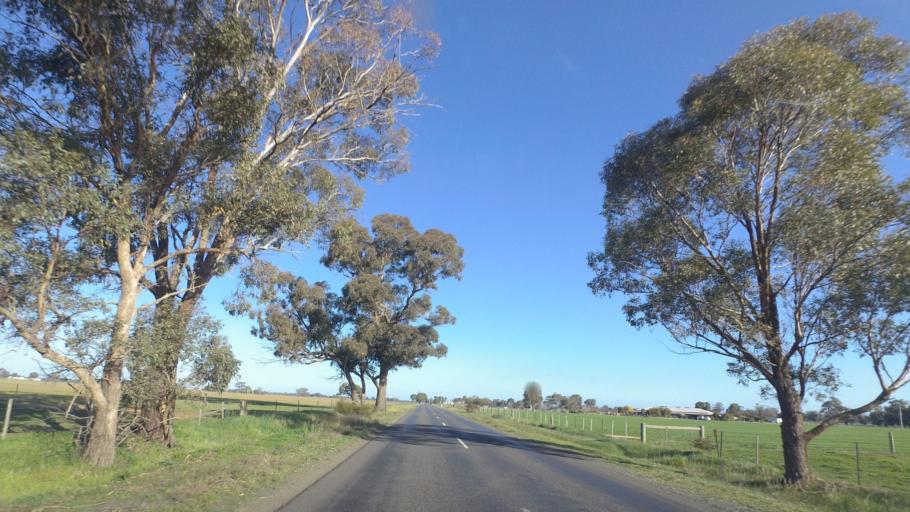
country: AU
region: Victoria
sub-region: Greater Bendigo
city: Epsom
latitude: -36.6103
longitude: 144.5351
